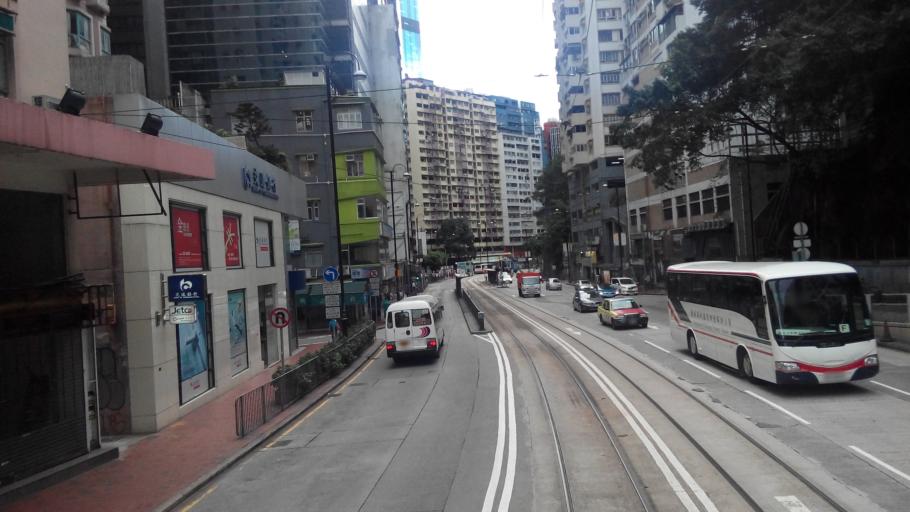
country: HK
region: Wanchai
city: Wan Chai
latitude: 22.2856
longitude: 114.1930
